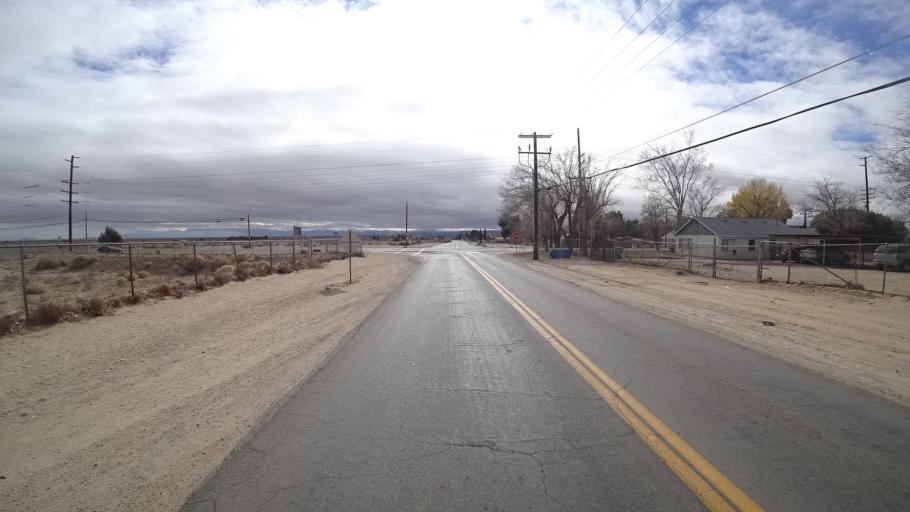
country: US
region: California
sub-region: Kern County
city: Rosamond
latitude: 34.8643
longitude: -118.2291
